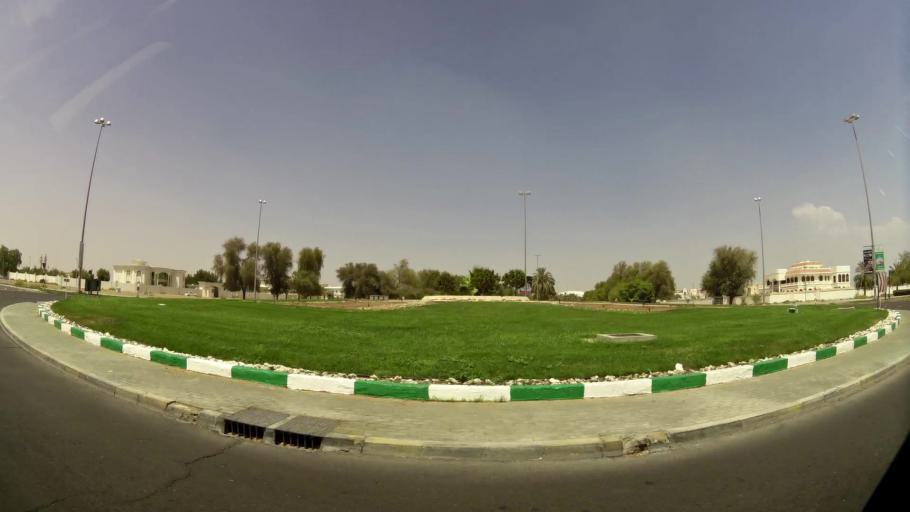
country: AE
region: Abu Dhabi
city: Al Ain
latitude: 24.2421
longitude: 55.7019
